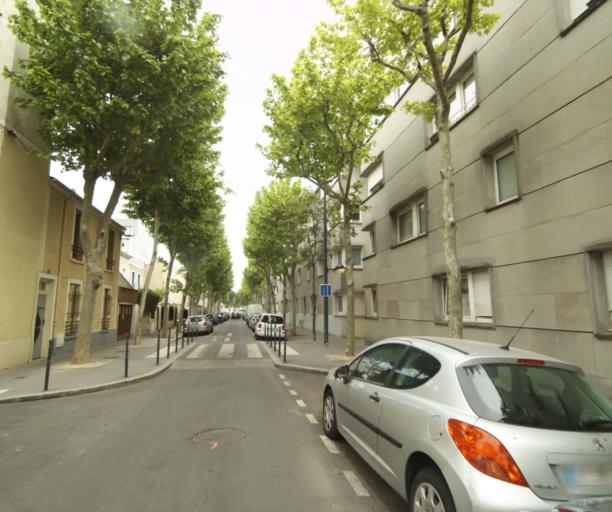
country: FR
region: Ile-de-France
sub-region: Departement des Hauts-de-Seine
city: Asnieres-sur-Seine
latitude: 48.9162
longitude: 2.2866
